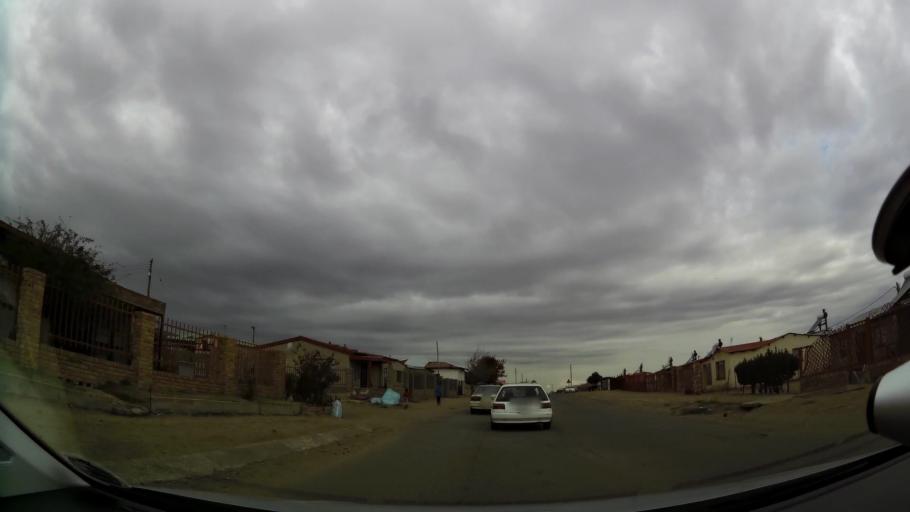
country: ZA
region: Orange Free State
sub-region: Fezile Dabi District Municipality
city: Kroonstad
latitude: -27.6521
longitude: 27.1914
